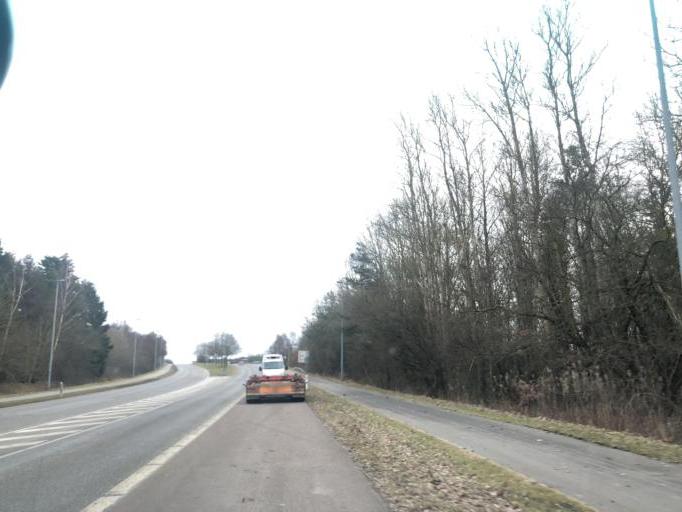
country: DK
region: Capital Region
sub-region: Vallensbaek Kommune
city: Vallensbaek
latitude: 55.6308
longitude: 12.3789
